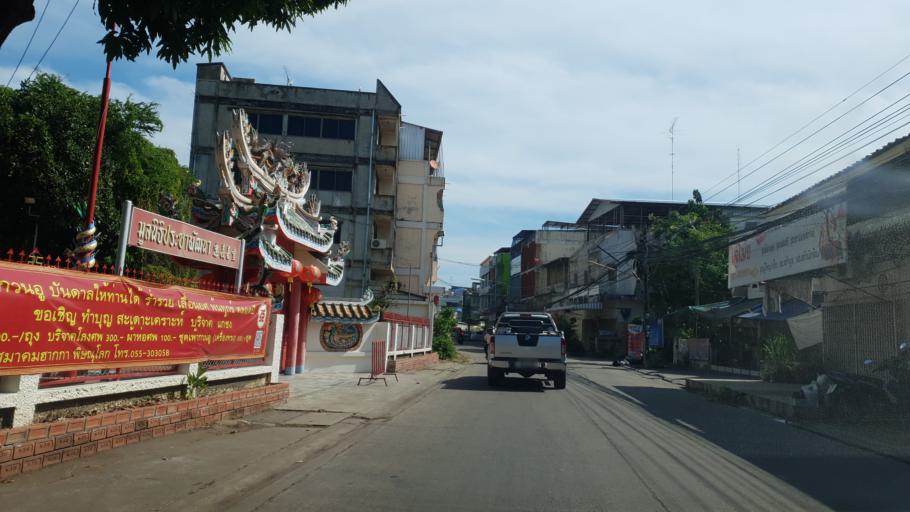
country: TH
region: Phitsanulok
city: Phitsanulok
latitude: 16.8146
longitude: 100.2699
